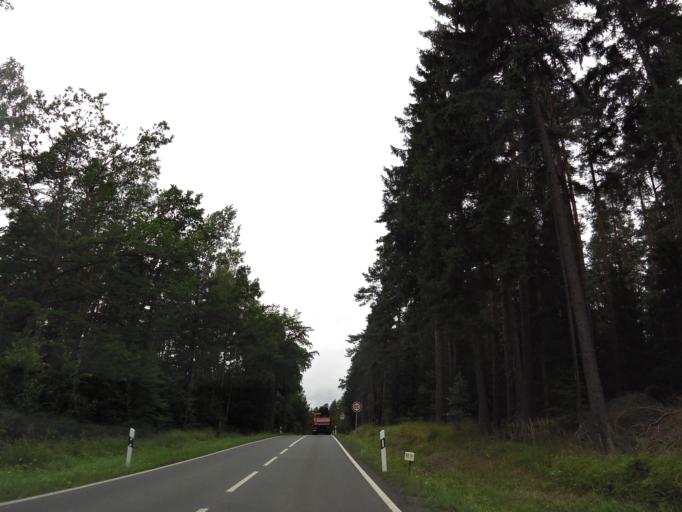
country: DE
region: Thuringia
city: Bad Klosterlausnitz
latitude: 50.9331
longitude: 11.8578
